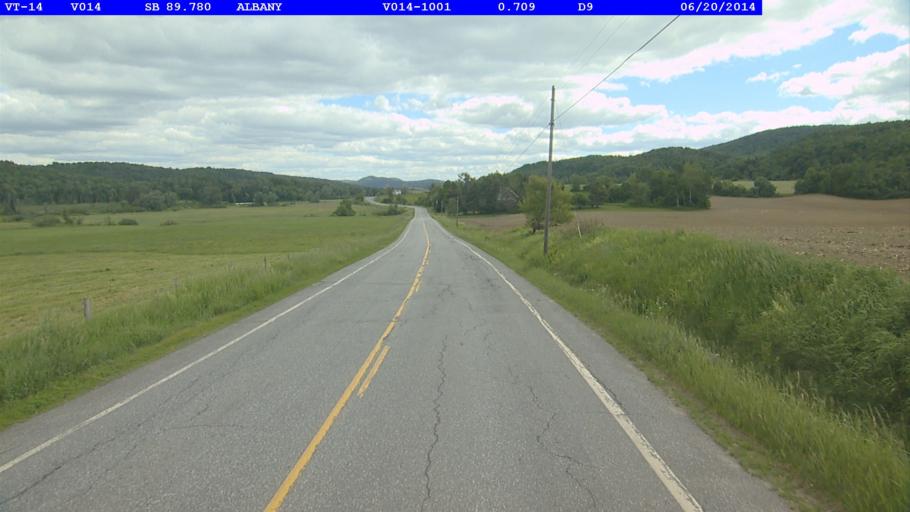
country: US
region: Vermont
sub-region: Caledonia County
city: Hardwick
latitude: 44.7127
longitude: -72.3886
